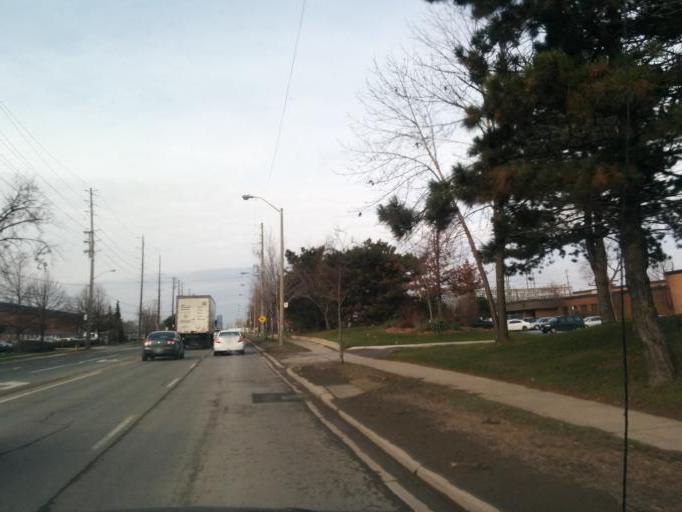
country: CA
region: Ontario
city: Etobicoke
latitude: 43.6080
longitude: -79.5210
